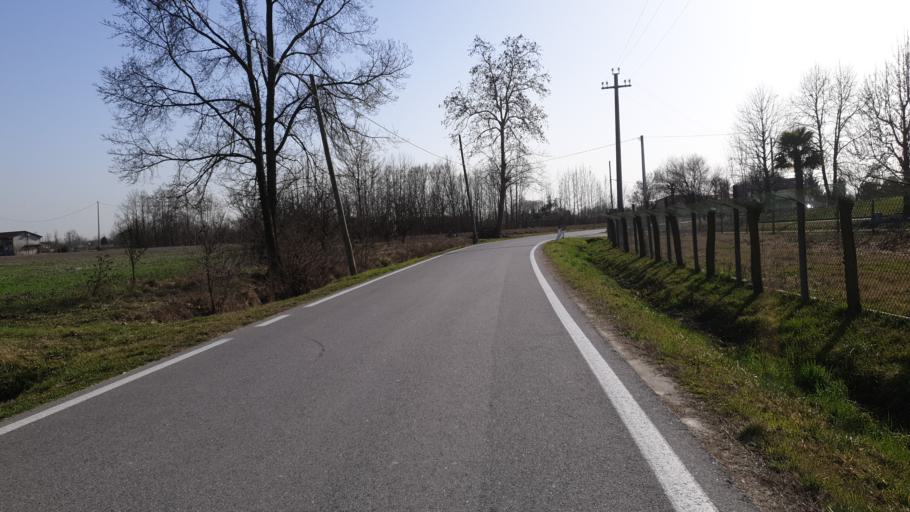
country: IT
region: Veneto
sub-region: Provincia di Padova
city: Tavo
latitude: 45.4906
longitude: 11.8837
